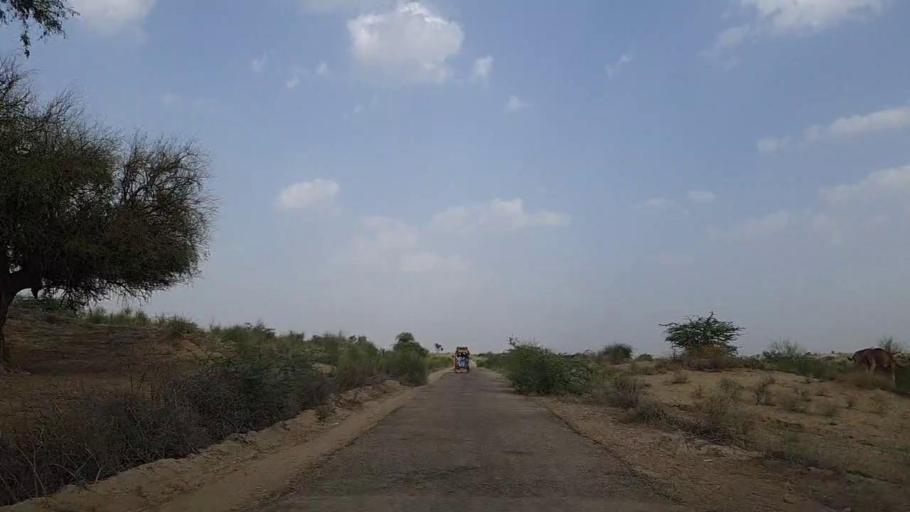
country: PK
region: Sindh
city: Islamkot
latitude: 24.7687
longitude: 70.1666
